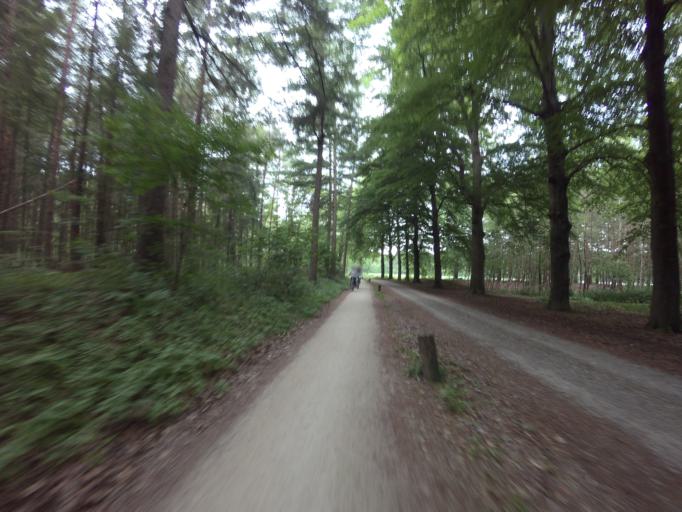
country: NL
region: North Holland
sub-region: Gemeente Hilversum
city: Hilversum
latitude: 52.1801
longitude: 5.2112
